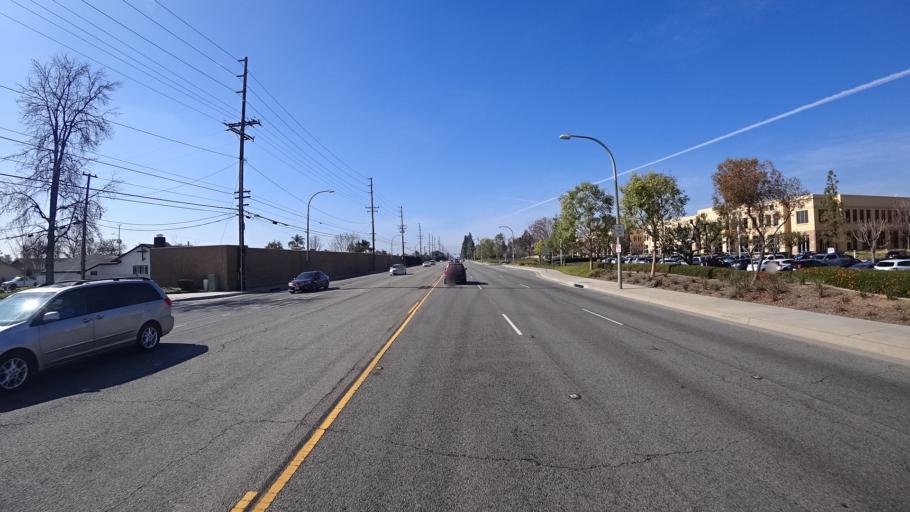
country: US
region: California
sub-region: Orange County
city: Brea
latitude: 33.9174
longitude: -117.9128
